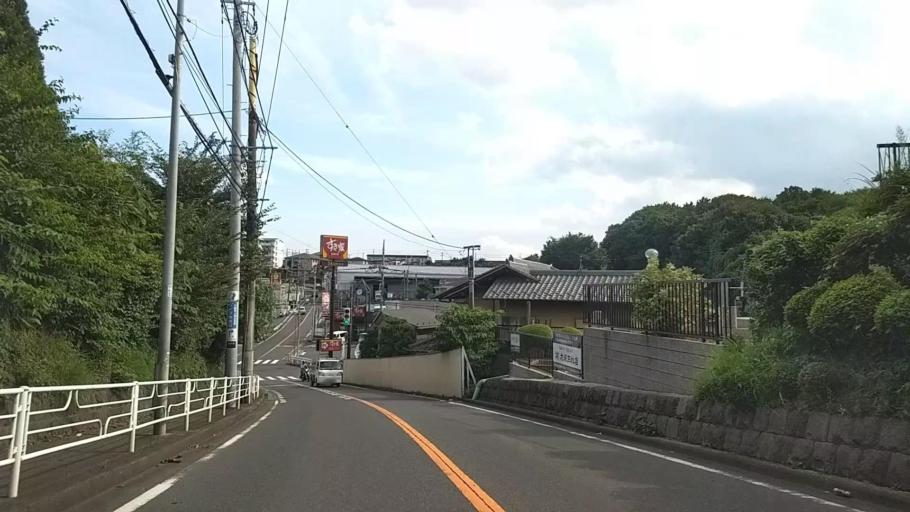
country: JP
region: Kanagawa
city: Yokohama
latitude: 35.4924
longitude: 139.5879
